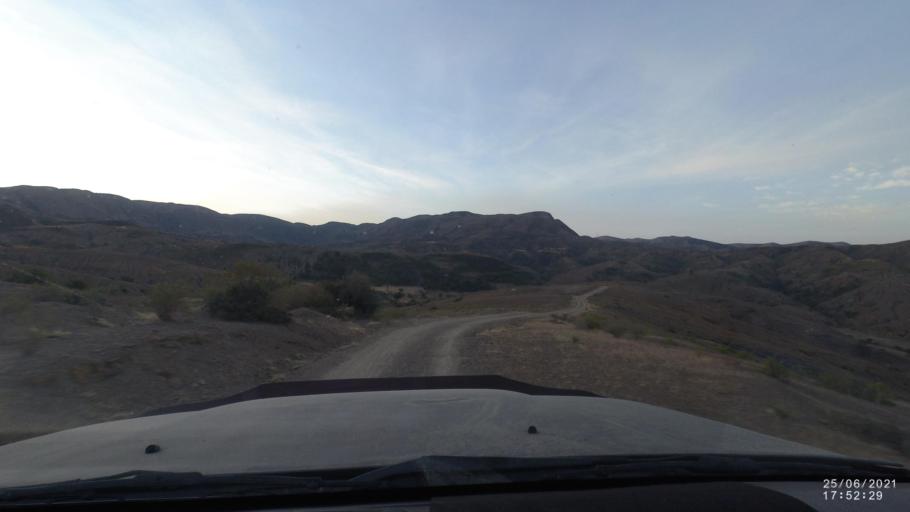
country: BO
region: Cochabamba
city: Mizque
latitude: -17.9475
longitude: -65.6405
